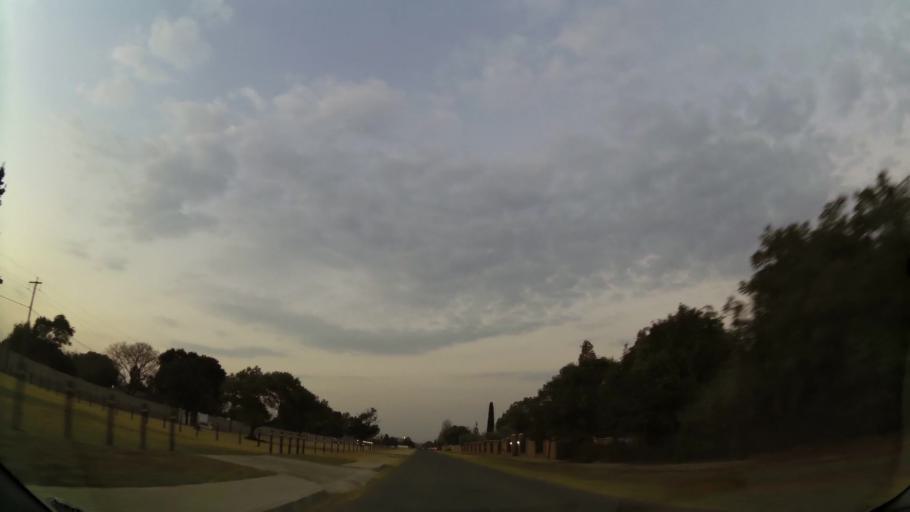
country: ZA
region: Gauteng
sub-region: Ekurhuleni Metropolitan Municipality
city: Benoni
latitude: -26.1410
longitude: 28.3110
